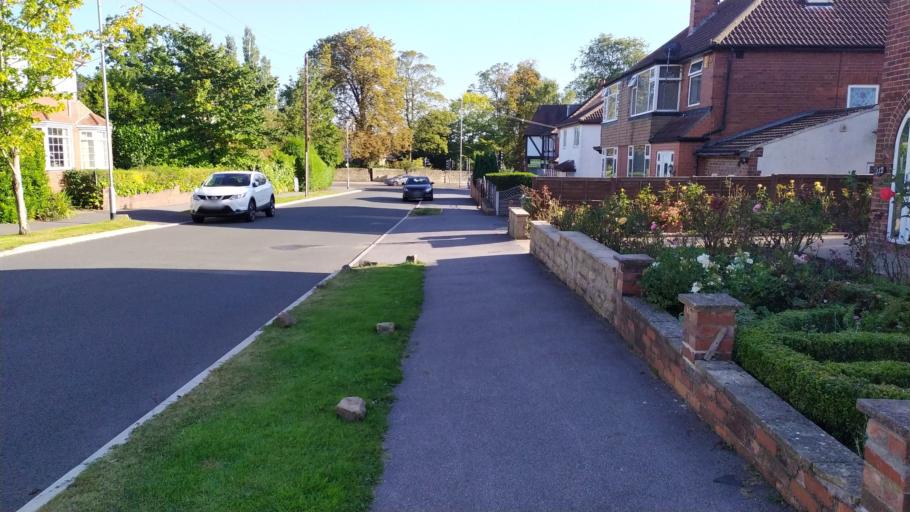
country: GB
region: England
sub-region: City and Borough of Leeds
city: Chapel Allerton
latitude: 53.8378
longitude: -1.5551
